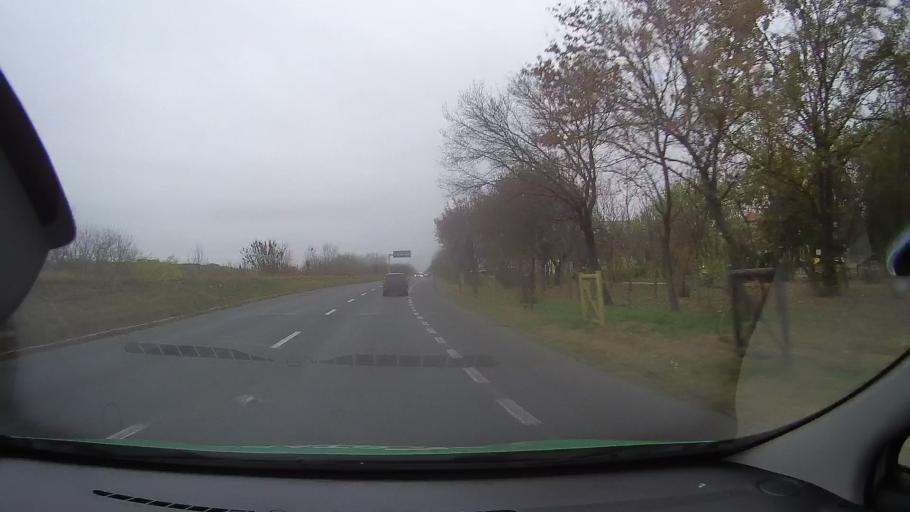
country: RO
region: Ialomita
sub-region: Comuna Slobozia
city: Slobozia
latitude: 44.5626
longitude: 27.3796
